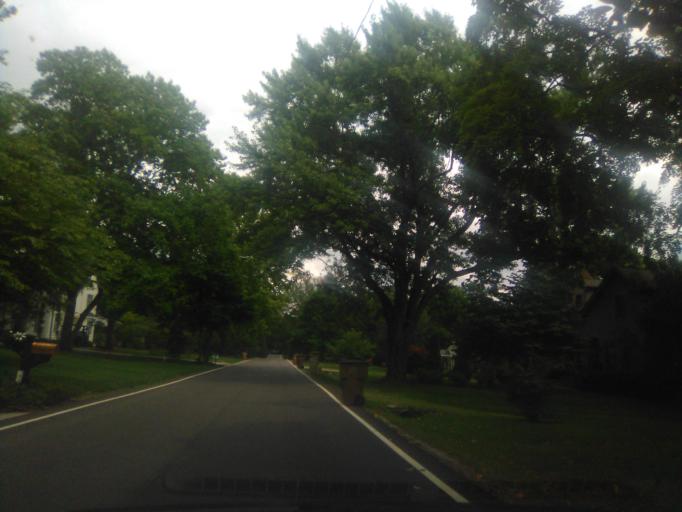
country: US
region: Tennessee
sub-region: Davidson County
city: Belle Meade
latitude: 36.0911
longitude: -86.8717
